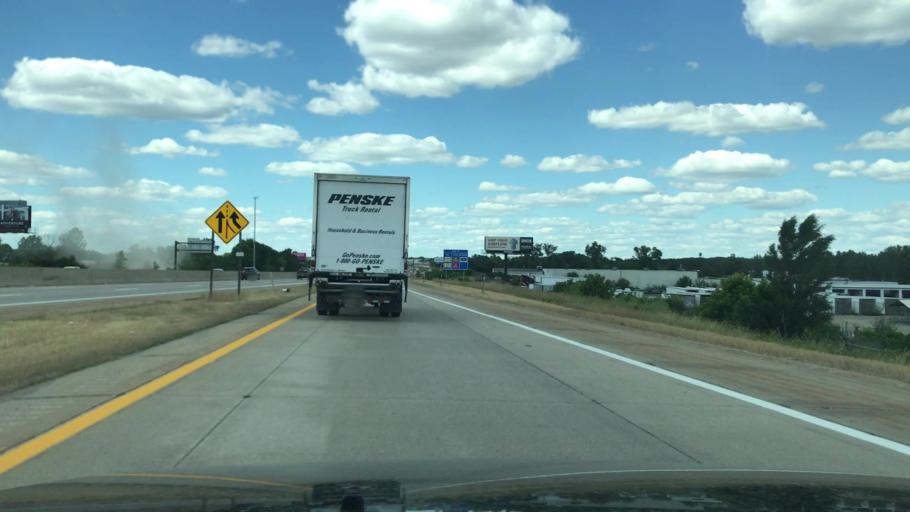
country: US
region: Michigan
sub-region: Kent County
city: Cutlerville
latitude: 42.8554
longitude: -85.6786
